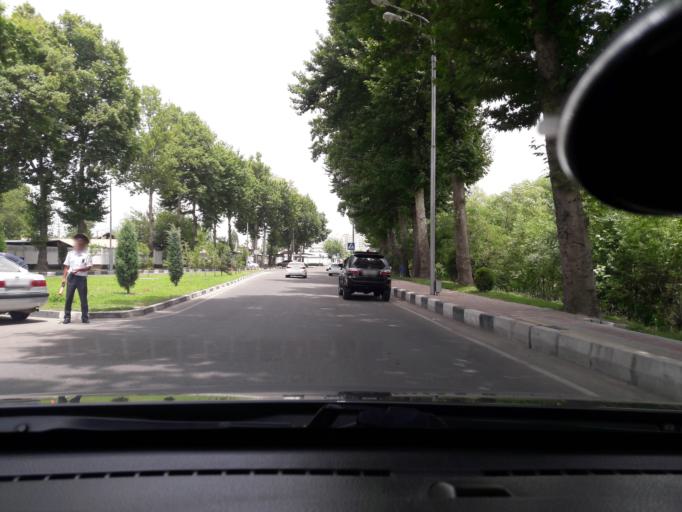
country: TJ
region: Dushanbe
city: Dushanbe
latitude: 38.5695
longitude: 68.7661
